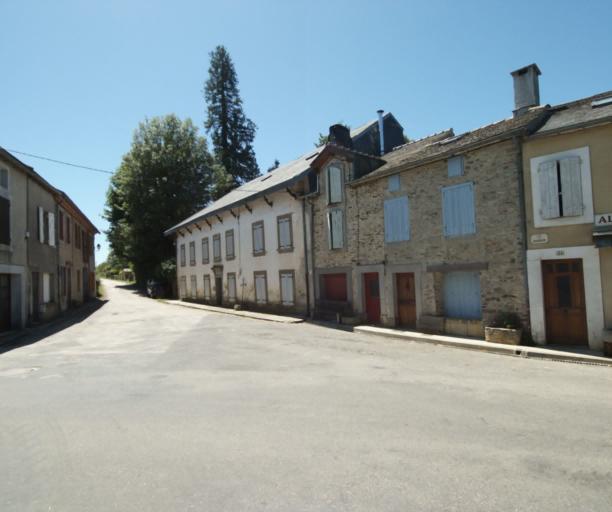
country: FR
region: Midi-Pyrenees
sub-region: Departement du Tarn
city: Dourgne
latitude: 43.4295
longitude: 2.1665
